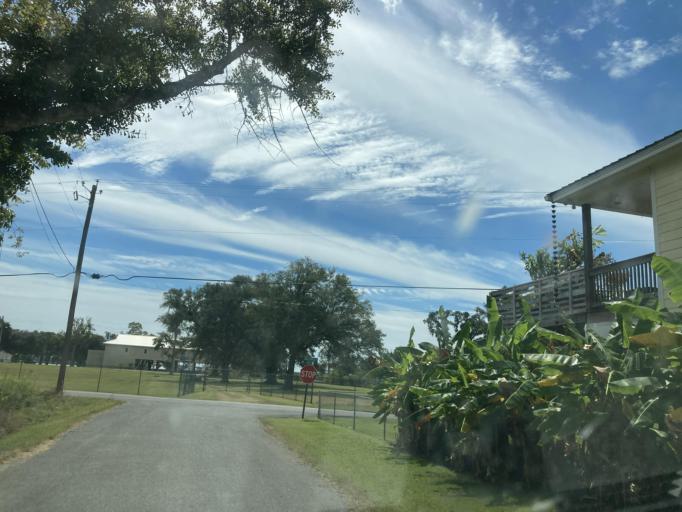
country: US
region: Mississippi
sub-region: Harrison County
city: D'Iberville
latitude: 30.4268
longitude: -88.8797
